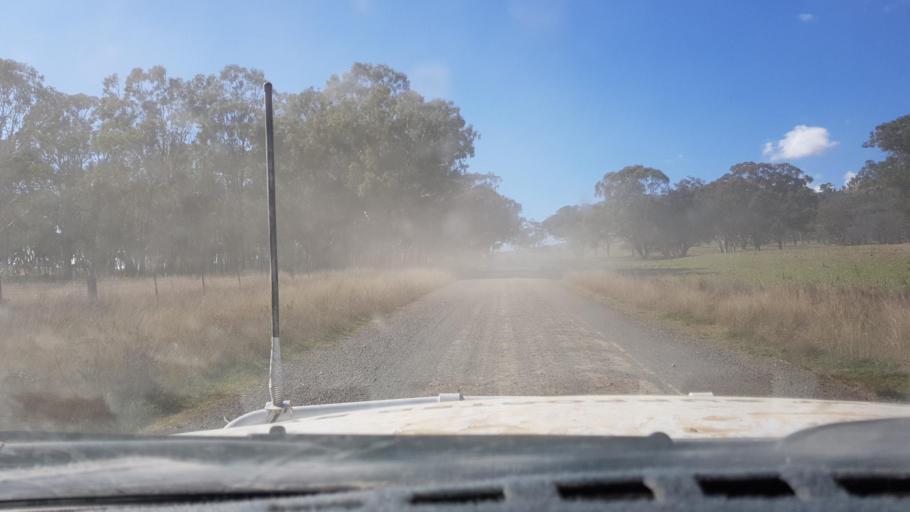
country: AU
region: New South Wales
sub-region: Narrabri
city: Blair Athol
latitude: -30.4191
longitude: 150.4616
